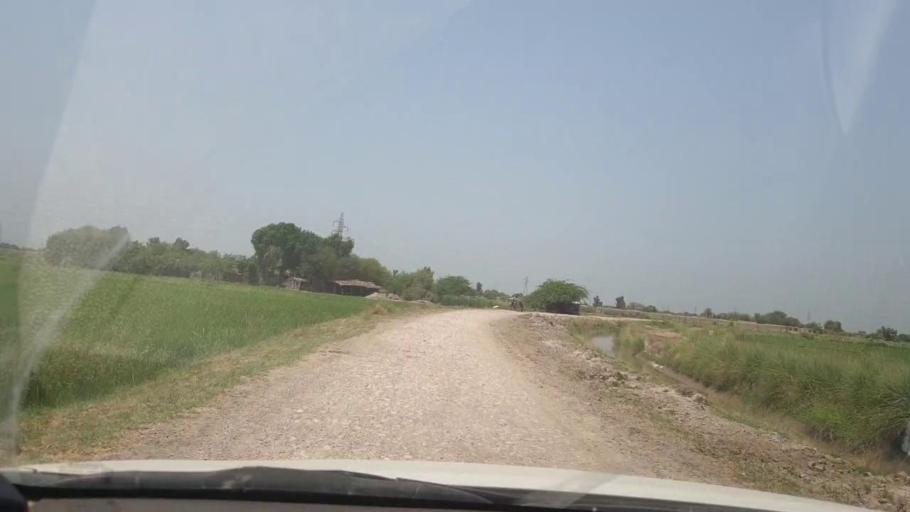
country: PK
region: Sindh
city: Lakhi
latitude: 27.8700
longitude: 68.6949
